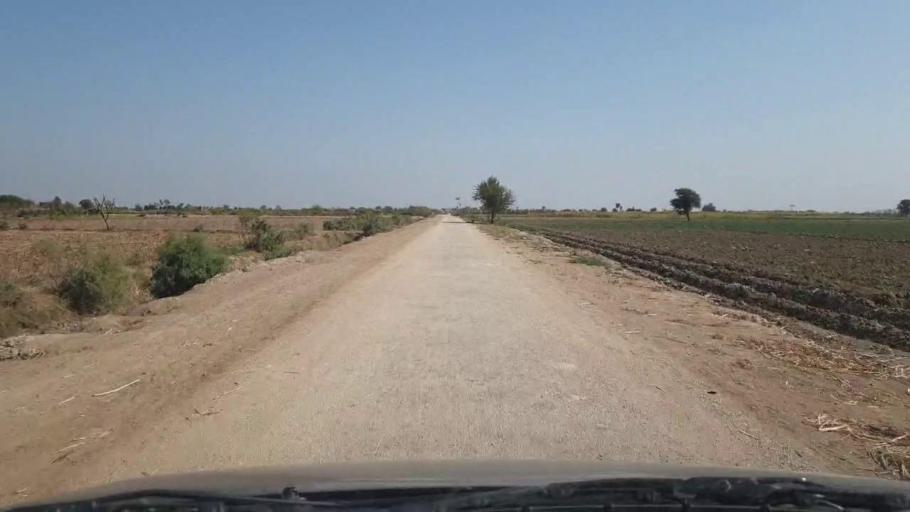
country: PK
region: Sindh
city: Samaro
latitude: 25.1967
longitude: 69.2969
